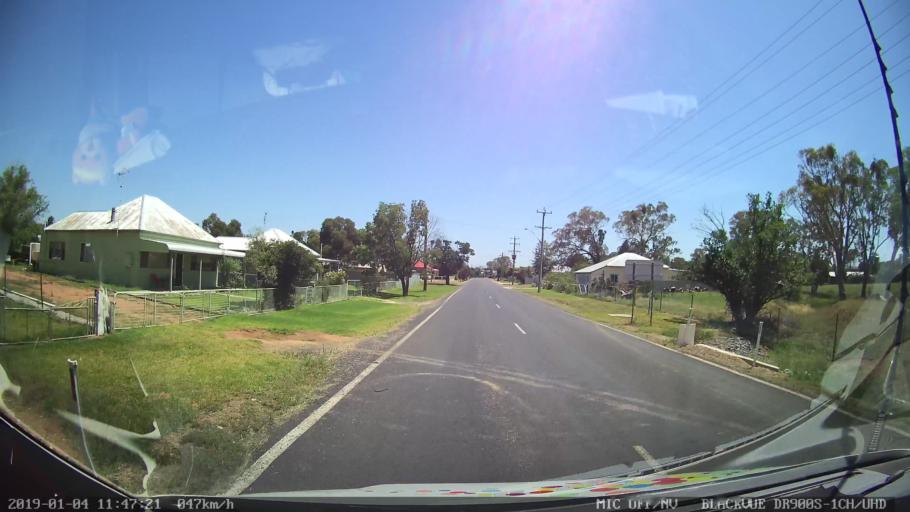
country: AU
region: New South Wales
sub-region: Cabonne
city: Molong
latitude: -32.9336
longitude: 148.7551
